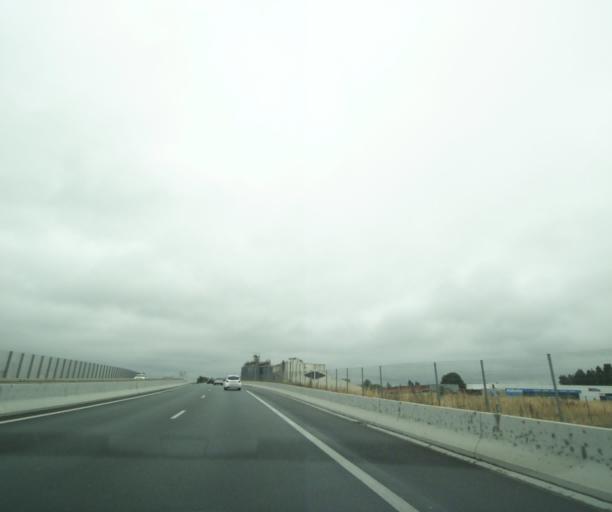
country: FR
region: Midi-Pyrenees
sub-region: Departement du Tarn
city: Puygouzon
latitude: 43.9174
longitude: 2.1647
